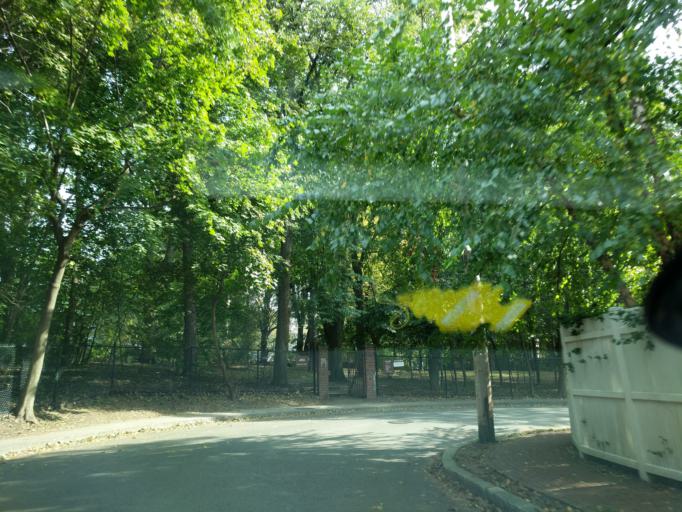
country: US
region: Massachusetts
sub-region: Middlesex County
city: Cambridge
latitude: 42.3809
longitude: -71.1113
